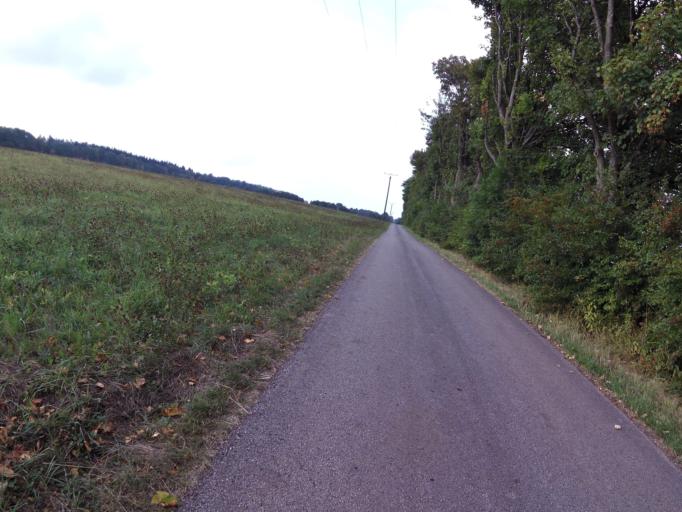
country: DE
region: North Rhine-Westphalia
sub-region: Regierungsbezirk Koln
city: Dahlem
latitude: 50.4214
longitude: 6.5876
